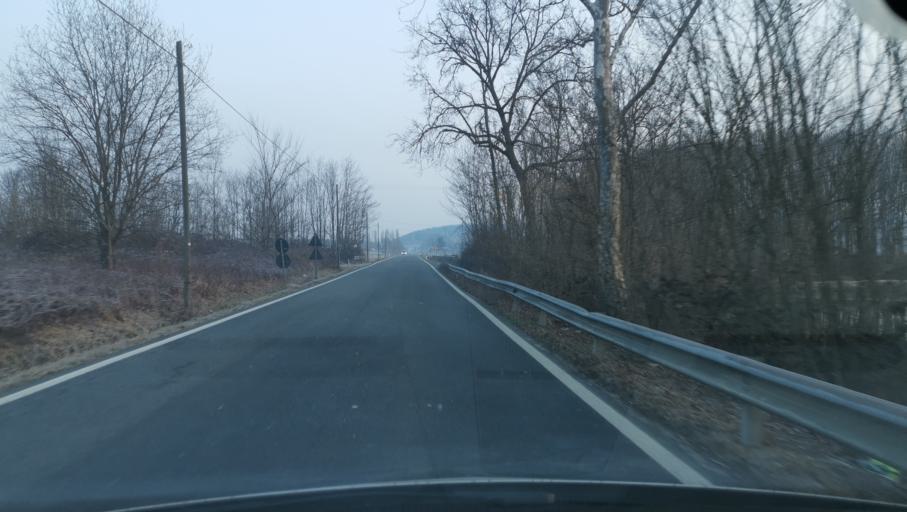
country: IT
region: Piedmont
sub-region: Provincia di Torino
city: San Giusto Canavese
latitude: 45.3186
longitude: 7.8296
